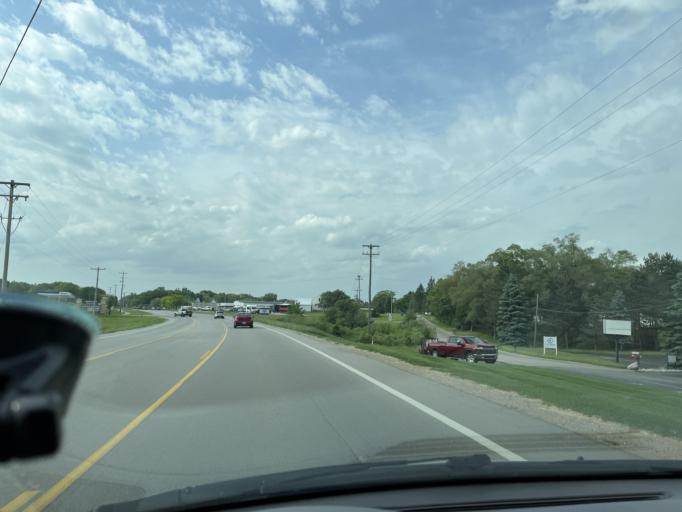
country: US
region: Michigan
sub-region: Barry County
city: Middleville
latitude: 42.7168
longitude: -85.4702
